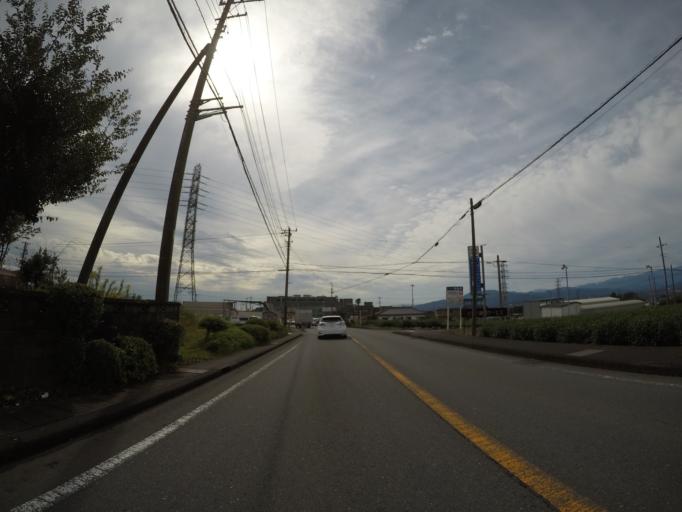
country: JP
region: Shizuoka
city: Fuji
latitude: 35.2069
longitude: 138.6847
